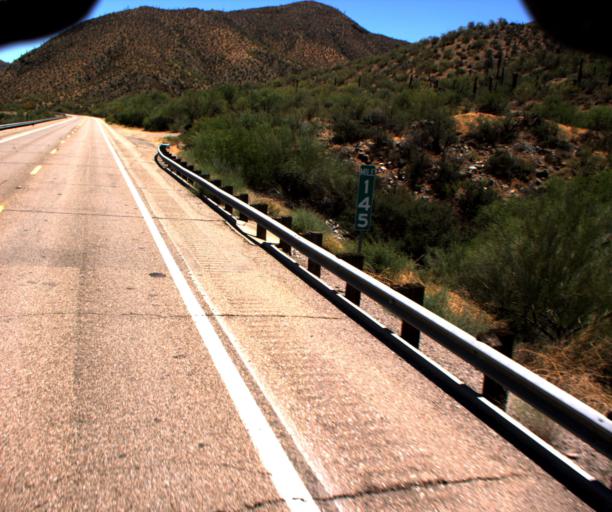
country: US
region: Arizona
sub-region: Pinal County
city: Kearny
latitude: 33.0639
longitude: -110.7247
